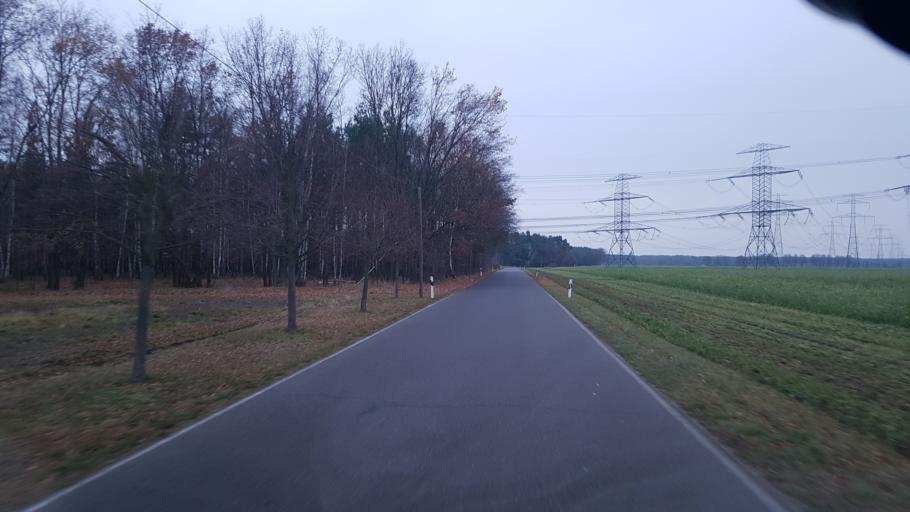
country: DE
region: Brandenburg
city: Peitz
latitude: 51.8771
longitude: 14.3975
